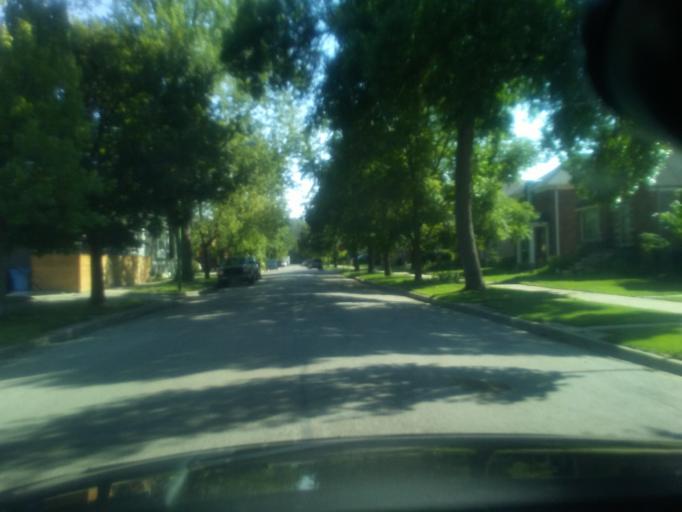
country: US
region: Illinois
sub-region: Cook County
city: Lincolnwood
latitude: 41.9852
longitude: -87.7384
